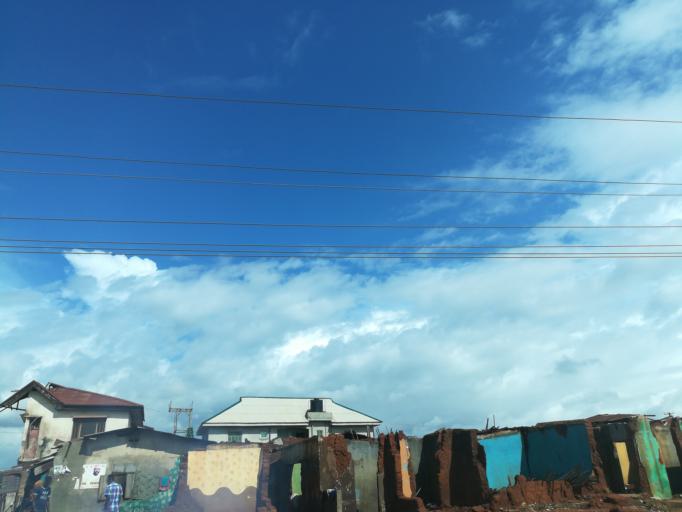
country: NG
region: Lagos
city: Ikorodu
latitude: 6.5919
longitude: 3.5180
